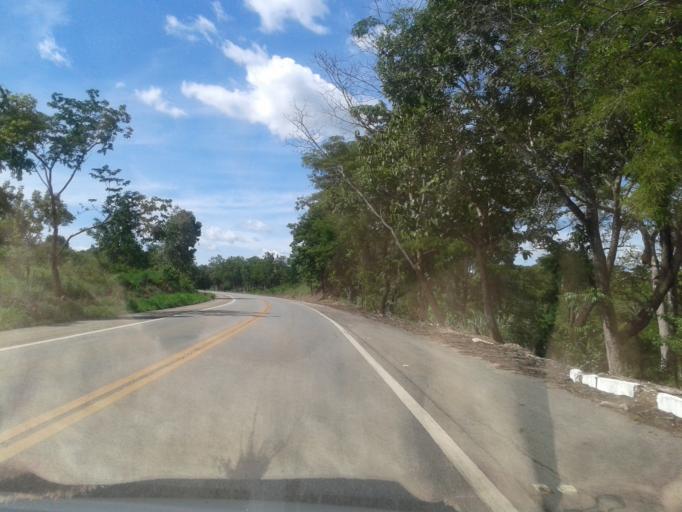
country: BR
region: Goias
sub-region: Itapuranga
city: Itapuranga
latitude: -15.4070
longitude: -50.3786
